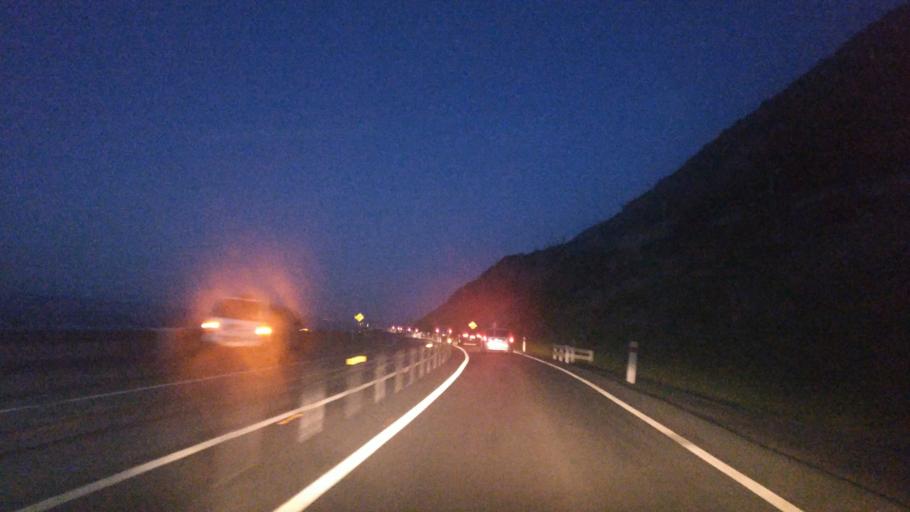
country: NZ
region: Wellington
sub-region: Porirua City
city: Porirua
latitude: -41.0174
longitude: 174.9148
